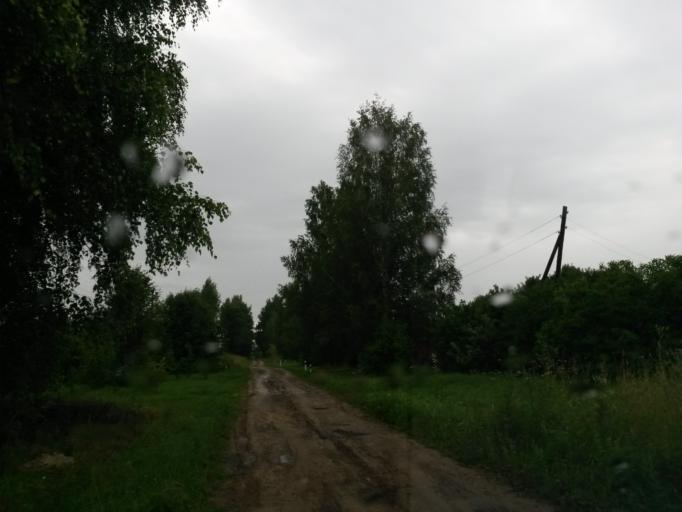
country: RU
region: Jaroslavl
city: Tutayev
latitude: 57.9447
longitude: 39.4413
